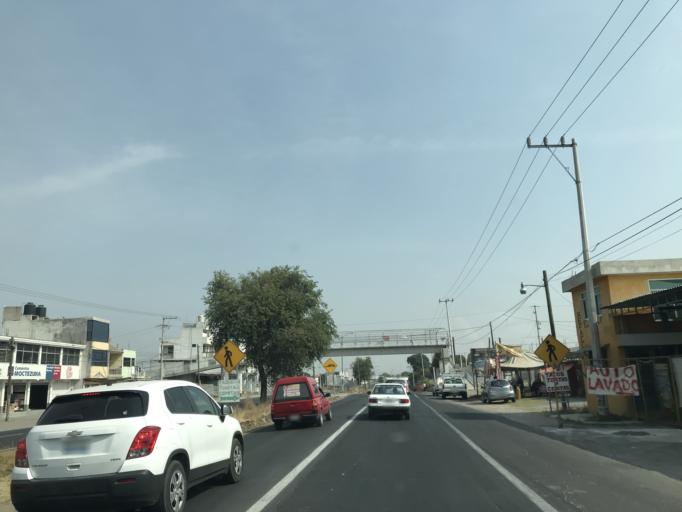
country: MX
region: Tlaxcala
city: Tenancingo
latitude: 19.1475
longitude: -98.1927
